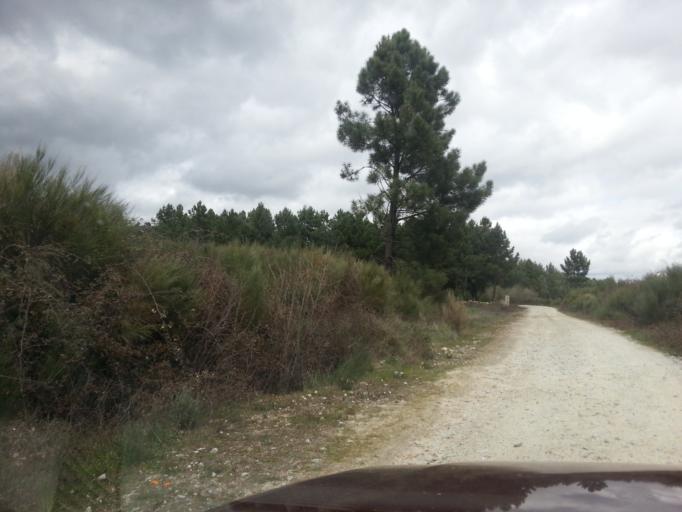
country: PT
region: Guarda
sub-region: Fornos de Algodres
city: Fornos de Algodres
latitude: 40.5996
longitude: -7.5614
